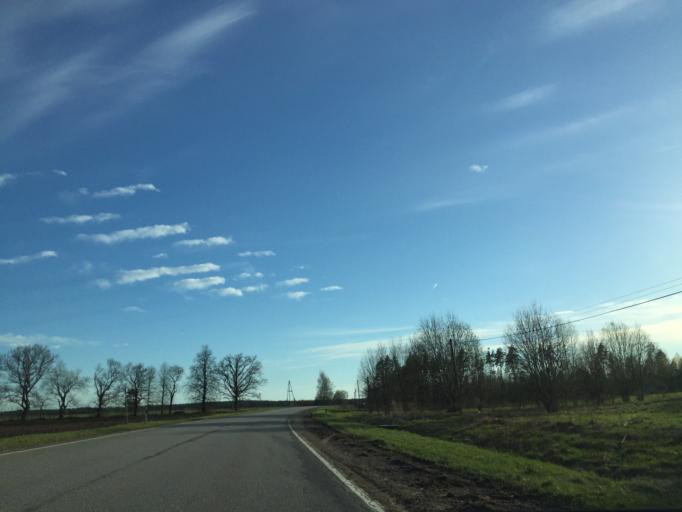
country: LV
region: Valkas Rajons
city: Valka
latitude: 57.7481
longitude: 25.9618
